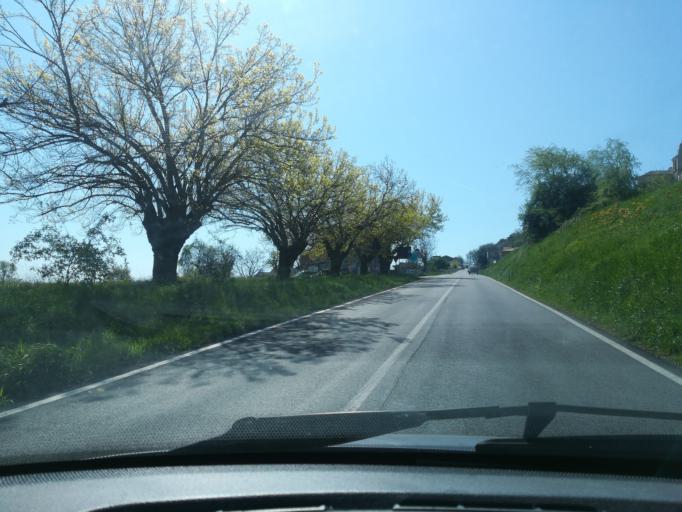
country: IT
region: The Marches
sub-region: Provincia di Macerata
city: Cingoli
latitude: 43.3784
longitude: 13.2161
